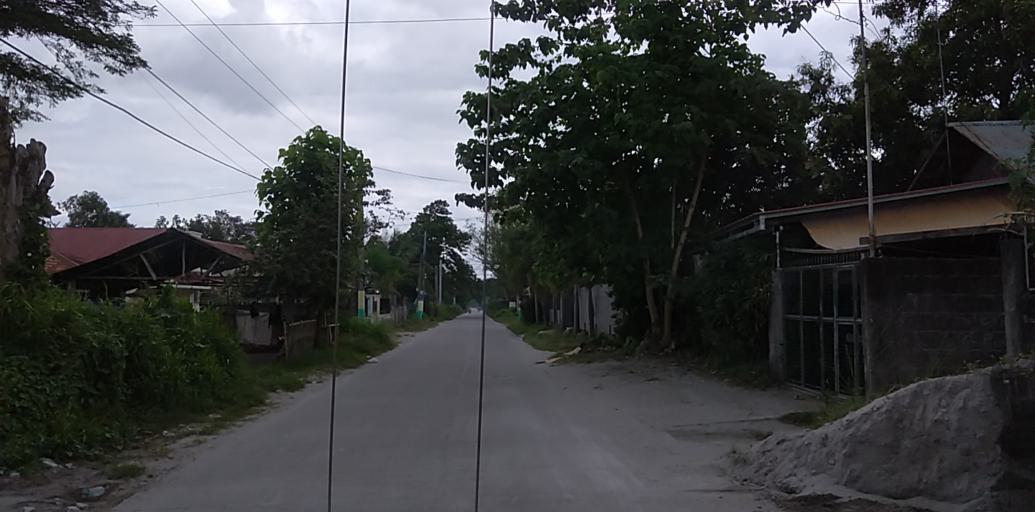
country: PH
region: Central Luzon
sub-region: Province of Pampanga
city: Porac
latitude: 15.0630
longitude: 120.5507
